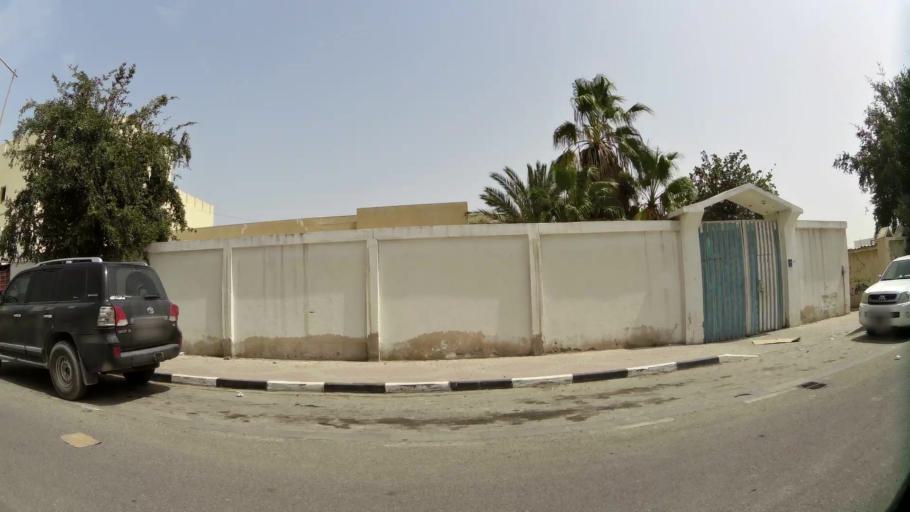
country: QA
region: Baladiyat ar Rayyan
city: Ar Rayyan
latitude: 25.2468
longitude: 51.4298
